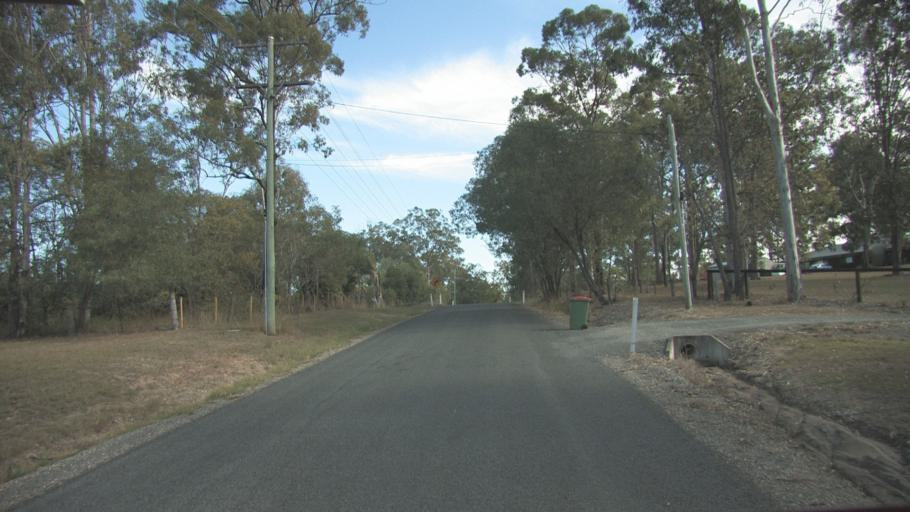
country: AU
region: Queensland
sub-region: Logan
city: North Maclean
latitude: -27.7725
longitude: 152.9701
